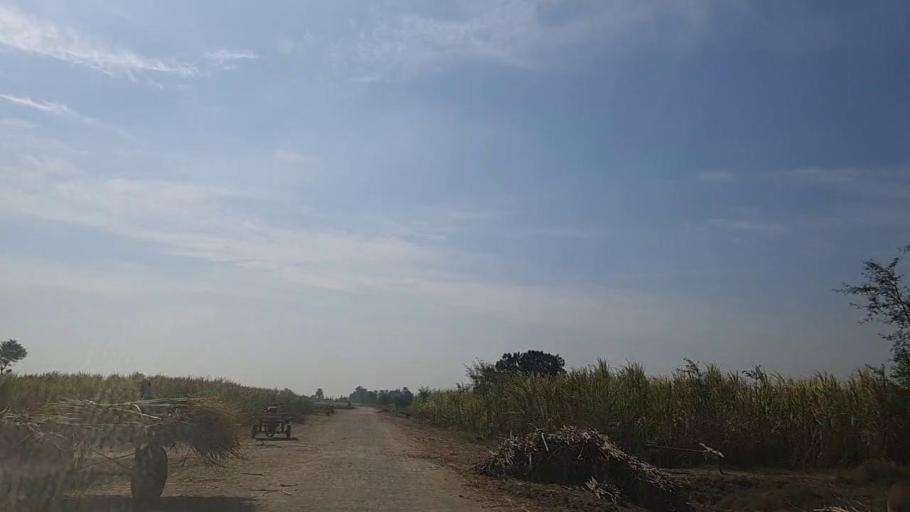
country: PK
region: Sindh
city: Mirpur Khas
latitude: 25.4741
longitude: 68.9640
